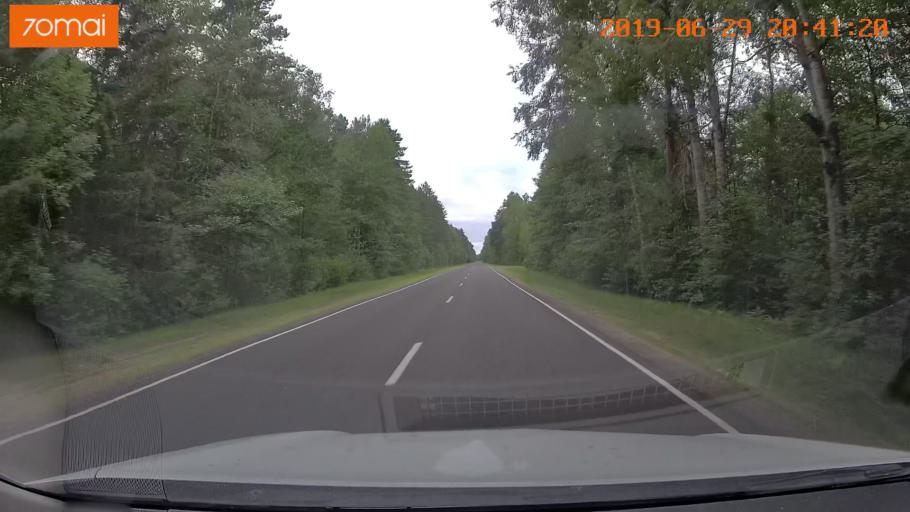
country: BY
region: Brest
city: Hantsavichy
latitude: 52.5845
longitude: 26.3408
